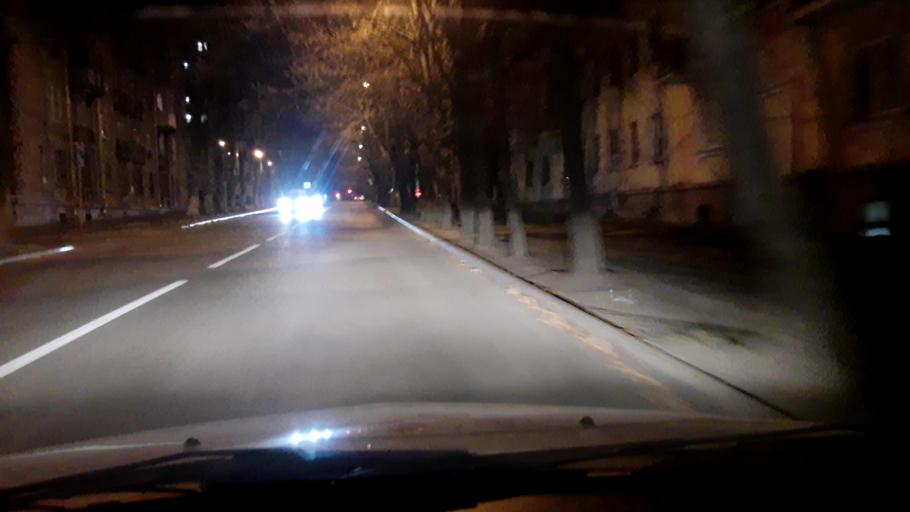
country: RU
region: Bashkortostan
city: Ufa
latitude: 54.8187
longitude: 56.0812
